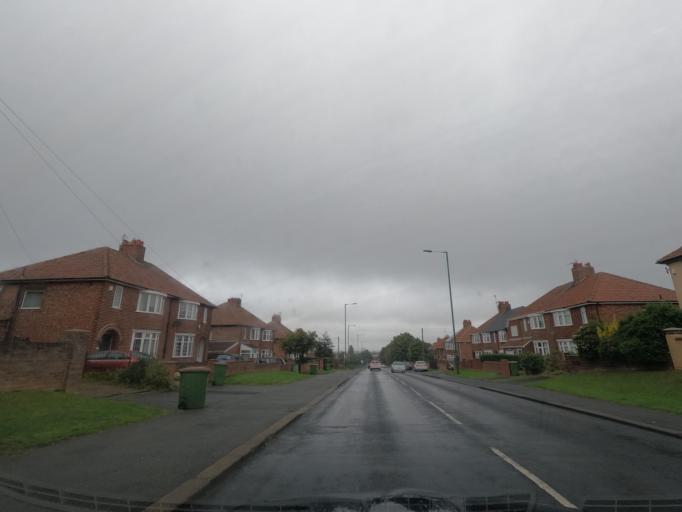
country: GB
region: England
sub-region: Middlesbrough
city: Nunthorpe
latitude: 54.5454
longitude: -1.1770
